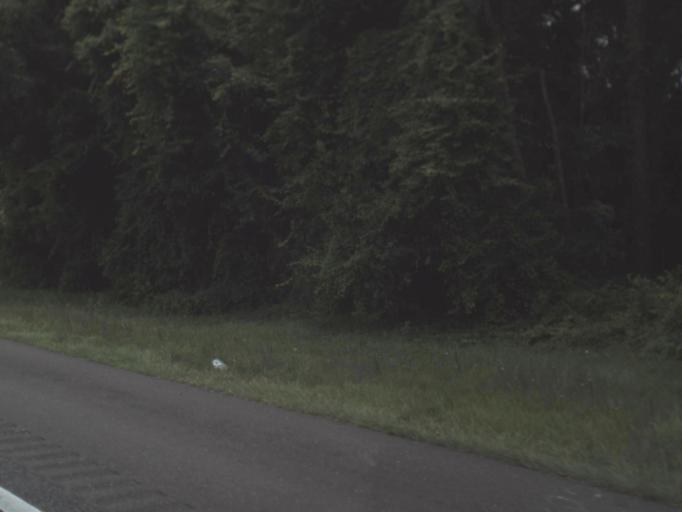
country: US
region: Florida
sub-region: Duval County
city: Jacksonville
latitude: 30.4415
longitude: -81.5910
